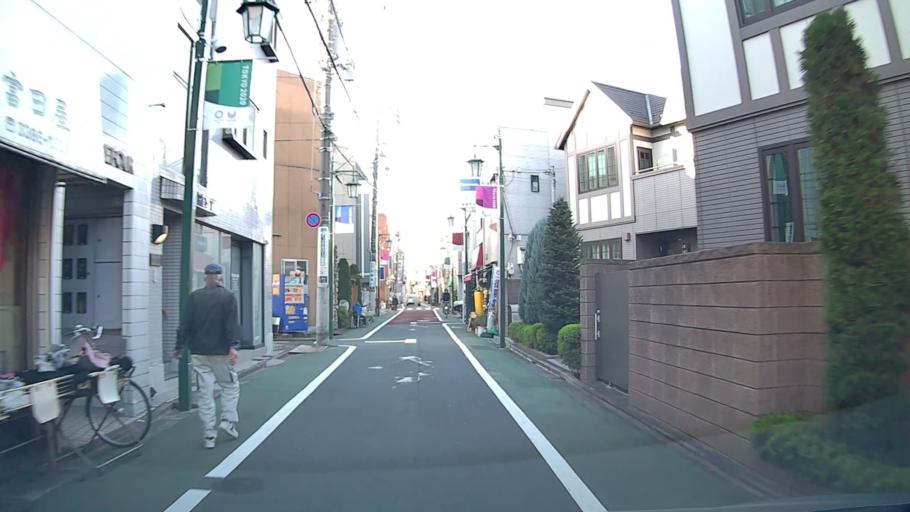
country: JP
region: Tokyo
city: Tokyo
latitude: 35.7133
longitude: 139.6730
